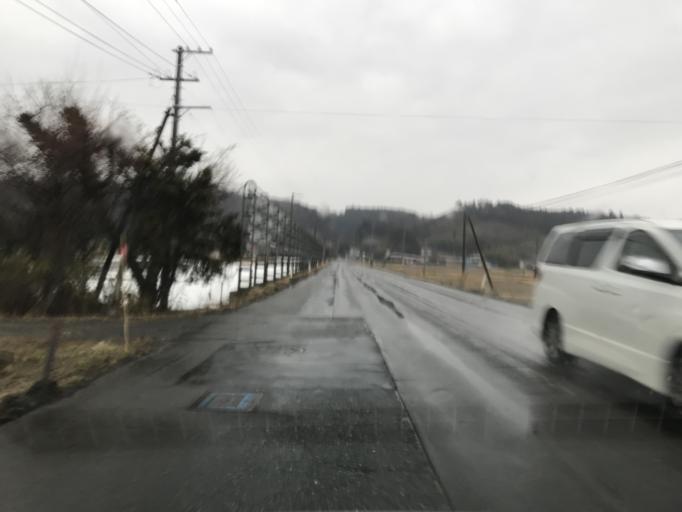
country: JP
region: Miyagi
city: Furukawa
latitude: 38.6729
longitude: 140.8700
